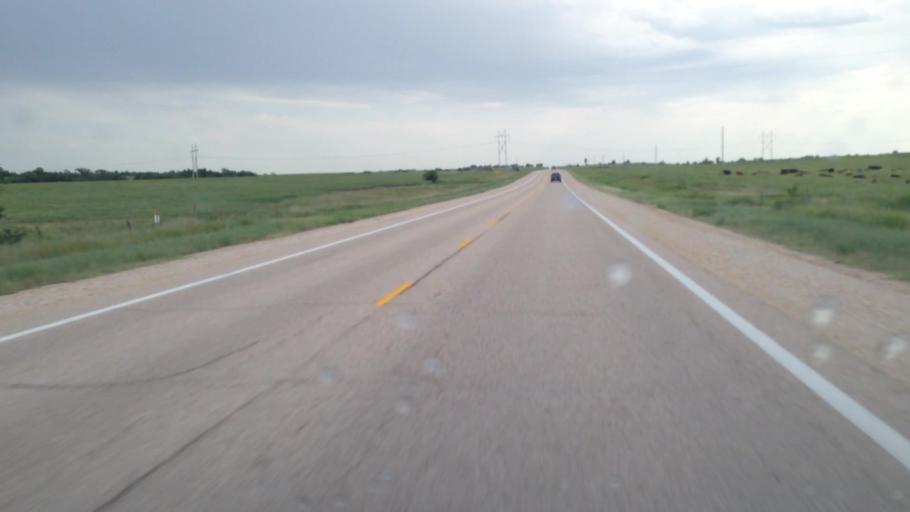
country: US
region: Kansas
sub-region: Coffey County
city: Burlington
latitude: 38.1631
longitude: -95.7390
